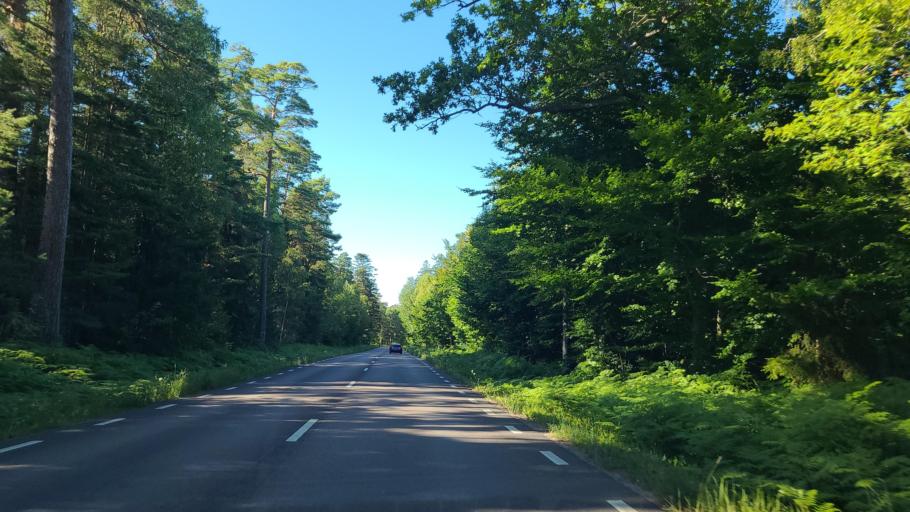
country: SE
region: Kalmar
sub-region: Borgholms Kommun
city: Borgholm
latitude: 57.2834
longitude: 17.0212
